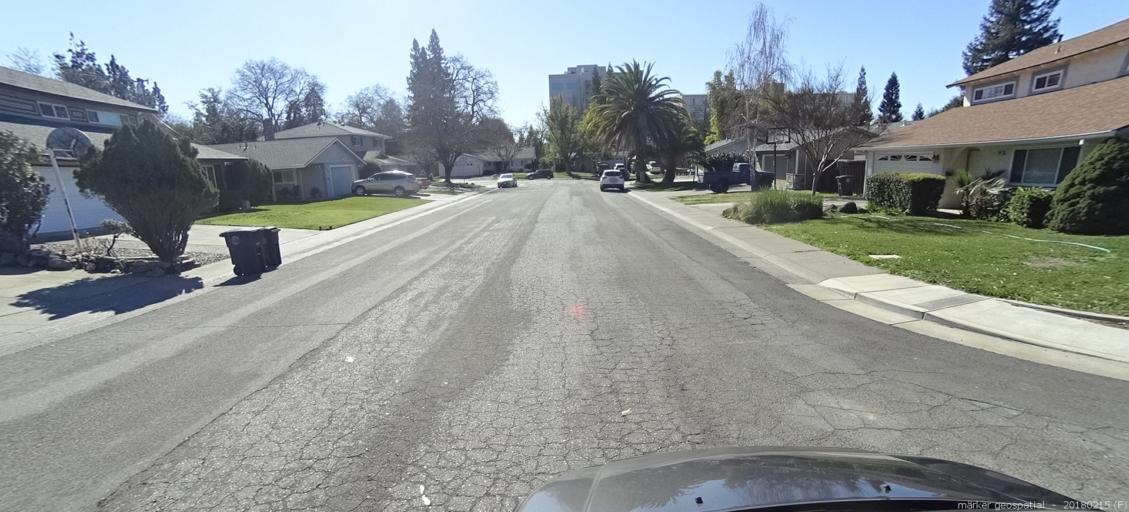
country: US
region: California
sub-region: Sacramento County
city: Foothill Farms
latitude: 38.6719
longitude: -121.3132
